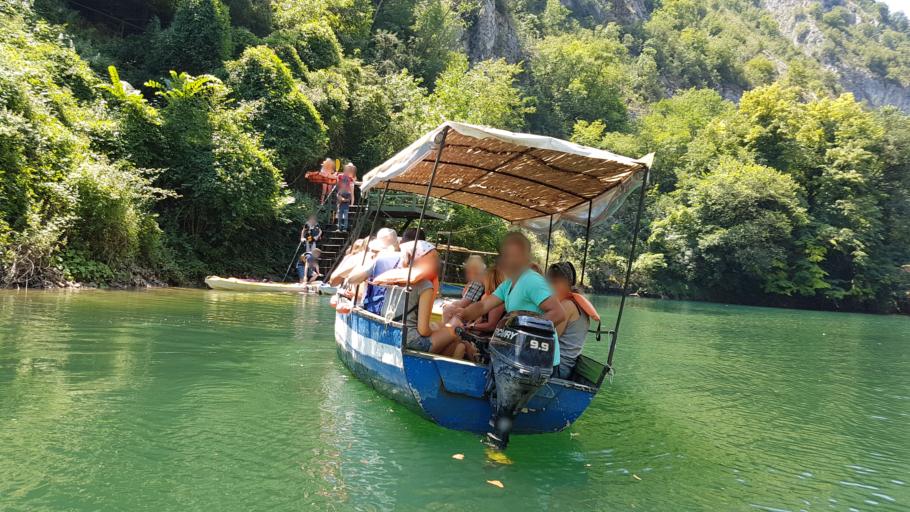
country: MK
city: Bukovik
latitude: 41.9306
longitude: 21.2922
